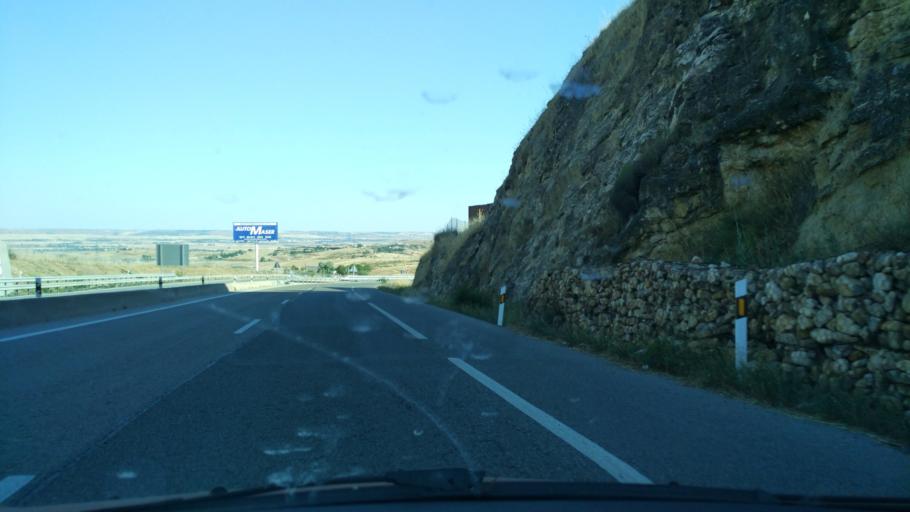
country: ES
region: Madrid
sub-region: Provincia de Madrid
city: El Molar
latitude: 40.7284
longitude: -3.5799
